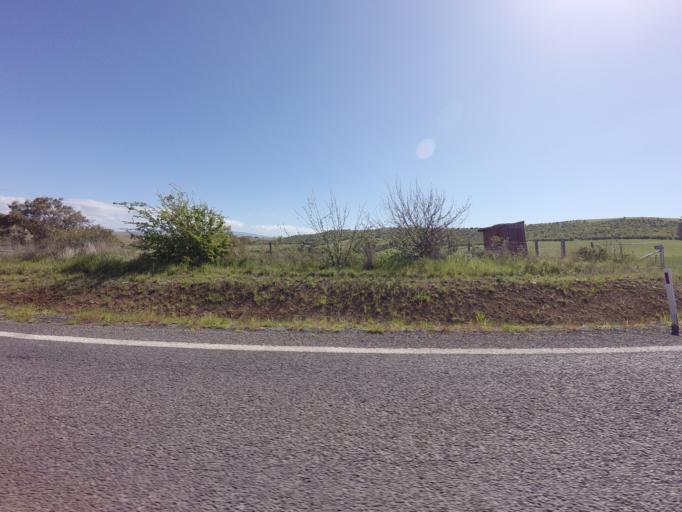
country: AU
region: Tasmania
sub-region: Derwent Valley
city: New Norfolk
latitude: -42.5688
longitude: 146.8808
